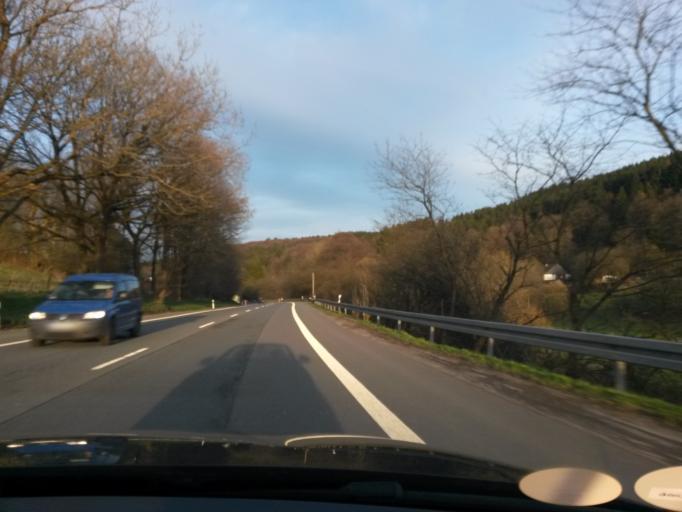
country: DE
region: North Rhine-Westphalia
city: Meinerzhagen
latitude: 51.1052
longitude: 7.7003
